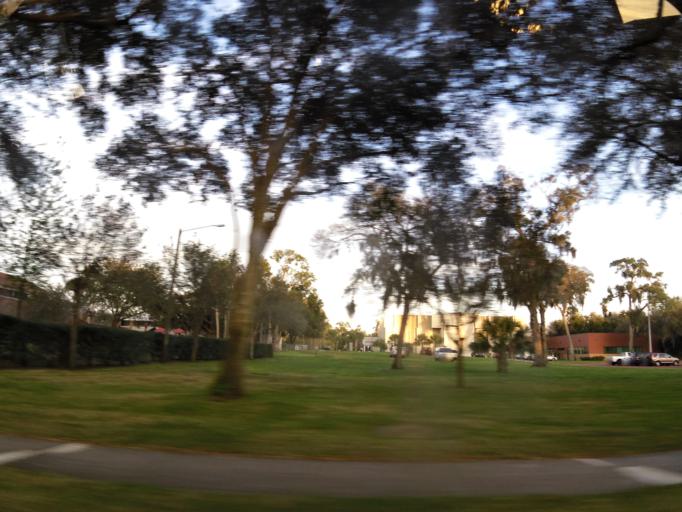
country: US
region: Florida
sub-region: Volusia County
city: North DeLand
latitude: 29.0398
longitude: -81.3038
